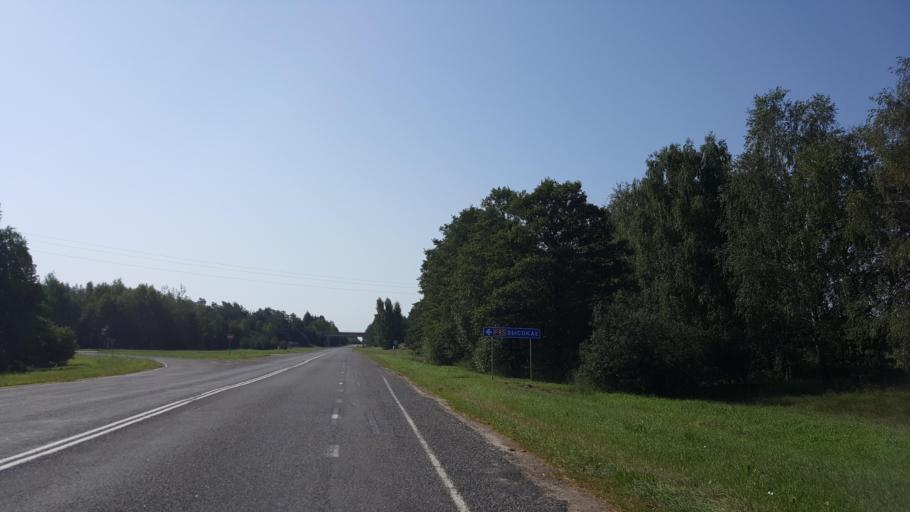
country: BY
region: Brest
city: Kamyanyets
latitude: 52.3451
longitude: 23.9041
